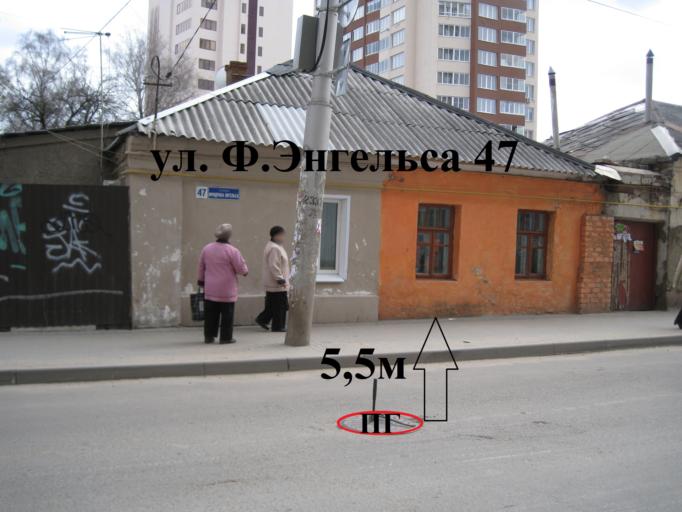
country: RU
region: Voronezj
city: Voronezh
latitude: 51.6627
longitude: 39.1936
